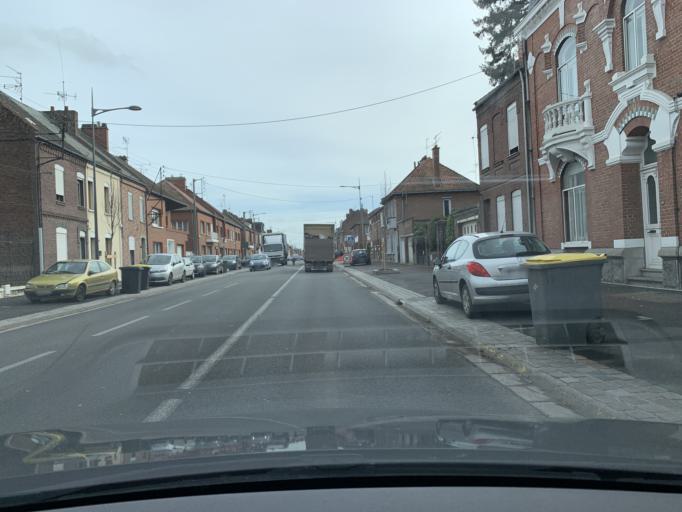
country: FR
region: Nord-Pas-de-Calais
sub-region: Departement du Nord
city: Cambrai
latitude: 50.1742
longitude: 3.2500
